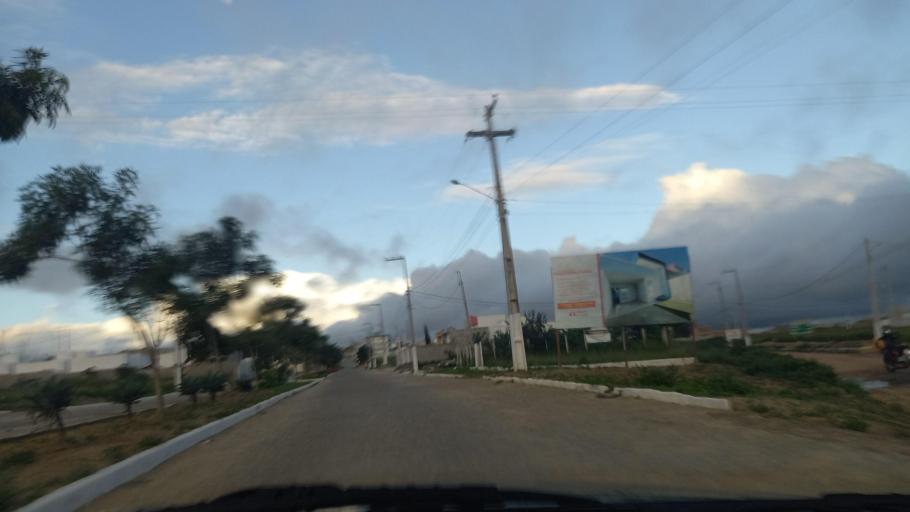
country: BR
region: Pernambuco
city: Garanhuns
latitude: -8.8923
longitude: -36.4436
